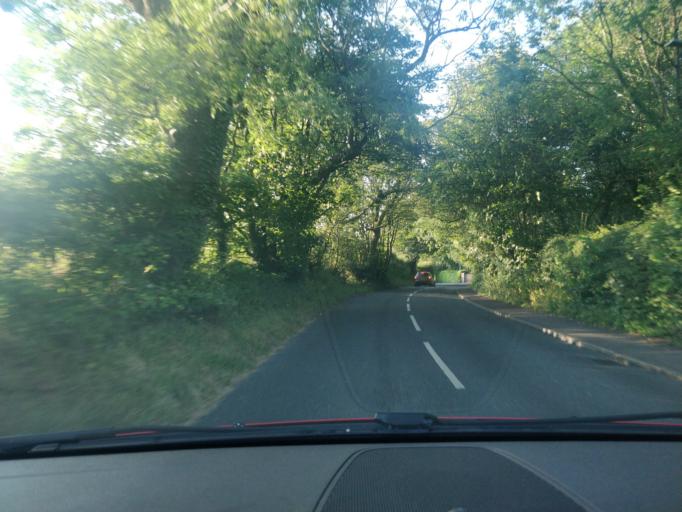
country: GB
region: England
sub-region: Lancashire
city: Skelmersdale
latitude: 53.5700
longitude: -2.7639
